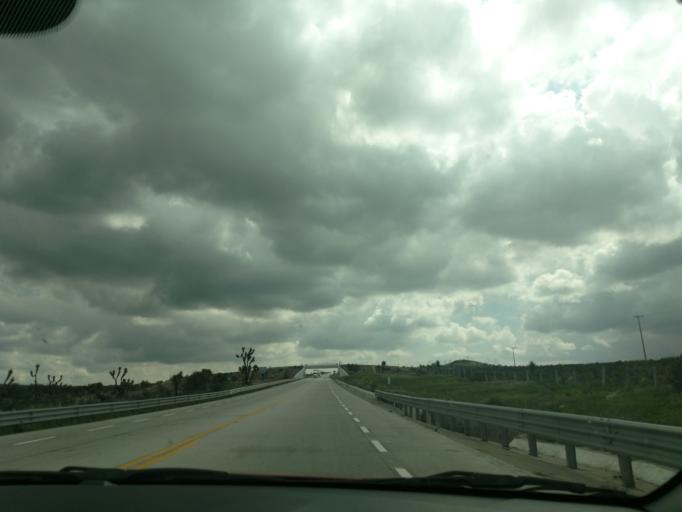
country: MX
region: Jalisco
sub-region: Ojuelos de Jalisco
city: Matanzas
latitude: 21.5663
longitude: -101.6800
